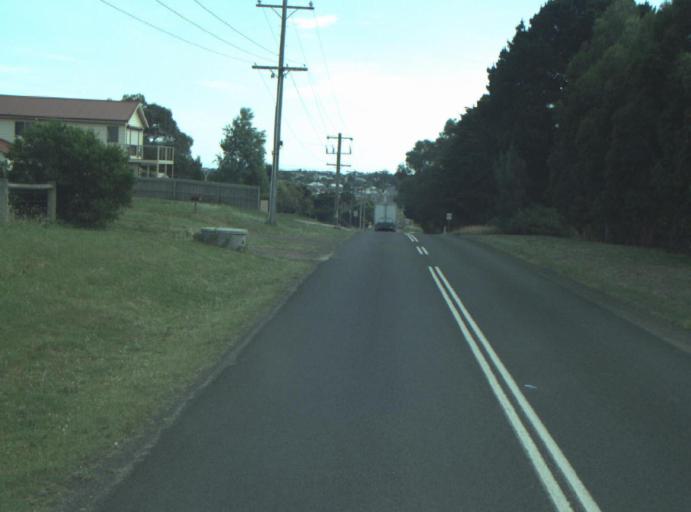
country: AU
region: Victoria
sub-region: Greater Geelong
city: Clifton Springs
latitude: -38.1861
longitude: 144.5683
